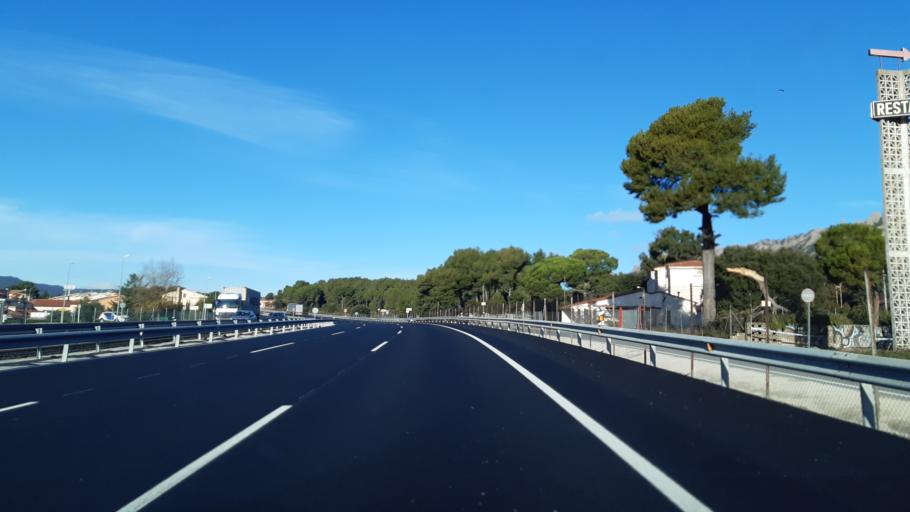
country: ES
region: Catalonia
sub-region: Provincia de Barcelona
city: Collbato
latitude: 41.5662
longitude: 1.8101
